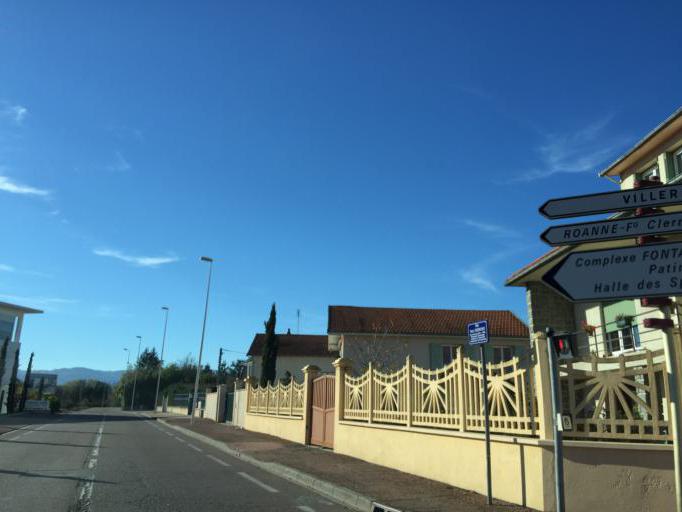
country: FR
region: Rhone-Alpes
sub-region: Departement de la Loire
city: Riorges
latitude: 46.0344
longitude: 4.0522
